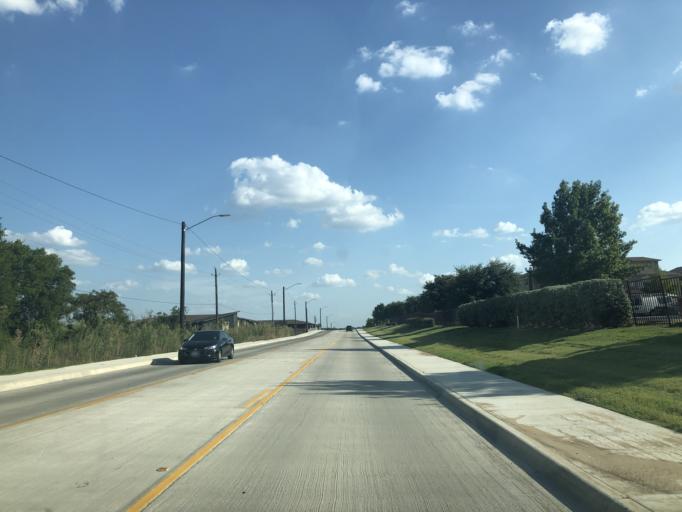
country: US
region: Texas
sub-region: Tarrant County
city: Sansom Park
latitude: 32.8223
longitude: -97.3795
